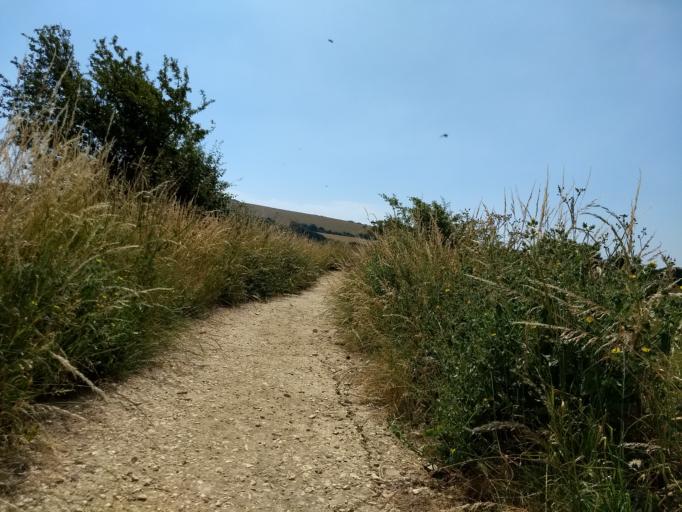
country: GB
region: England
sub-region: Isle of Wight
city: Brading
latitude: 50.6805
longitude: -1.1301
